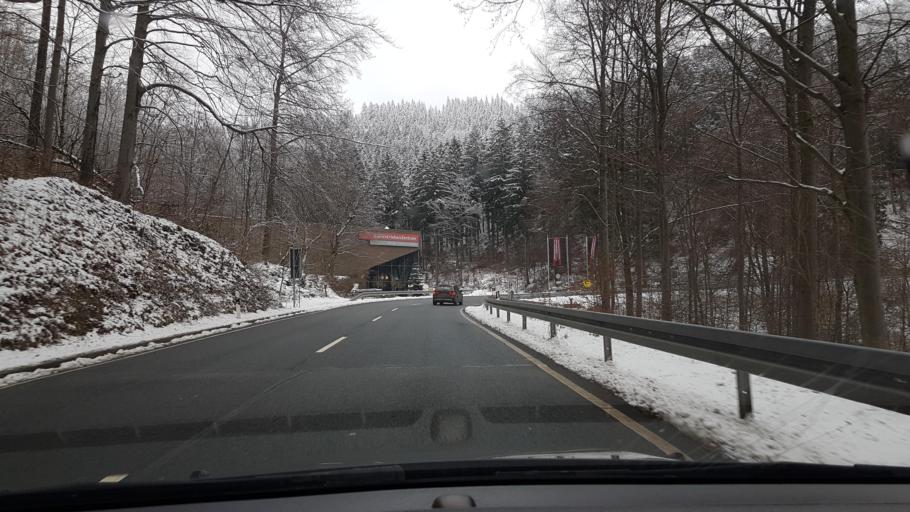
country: DE
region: Lower Saxony
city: Bad Grund
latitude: 51.8168
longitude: 10.2517
